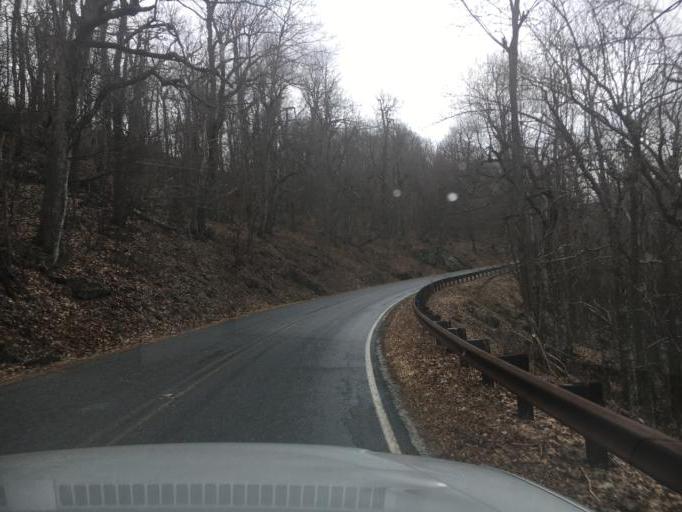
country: US
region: North Carolina
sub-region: Transylvania County
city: Brevard
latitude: 35.3688
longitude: -82.7903
